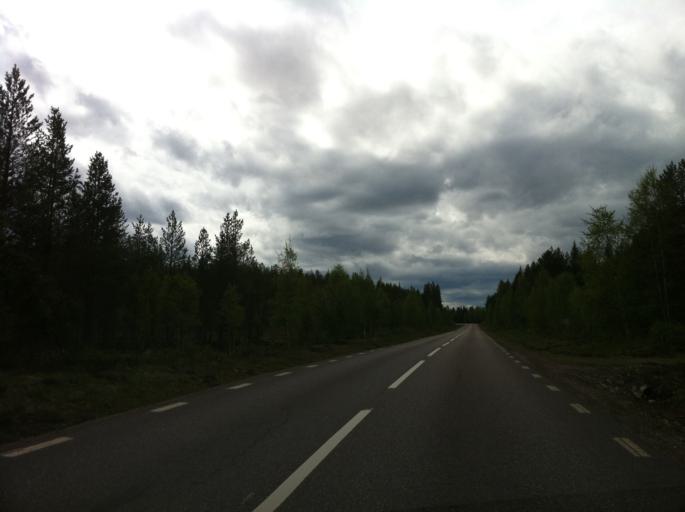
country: NO
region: Hedmark
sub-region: Trysil
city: Innbygda
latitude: 61.5688
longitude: 13.1001
